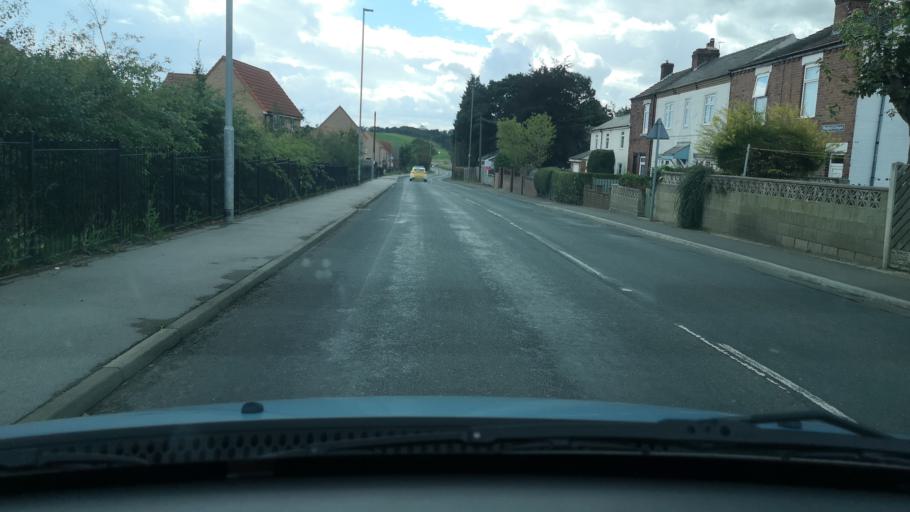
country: GB
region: England
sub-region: City and Borough of Wakefield
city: Pontefract
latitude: 53.6770
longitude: -1.3162
